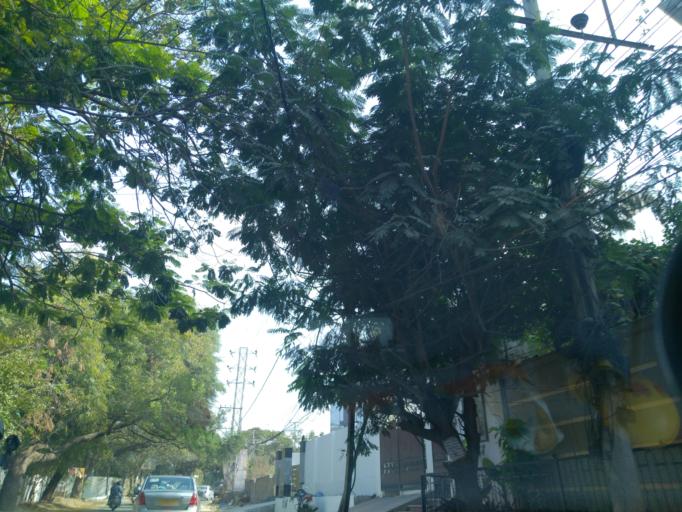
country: IN
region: Telangana
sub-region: Rangareddi
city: Kukatpalli
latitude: 17.4329
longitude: 78.4017
